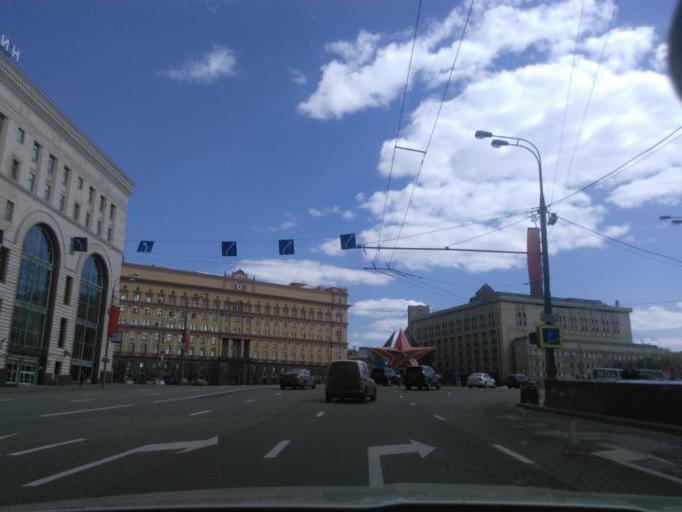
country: RU
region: Moscow
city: Moscow
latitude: 55.7594
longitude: 37.6246
